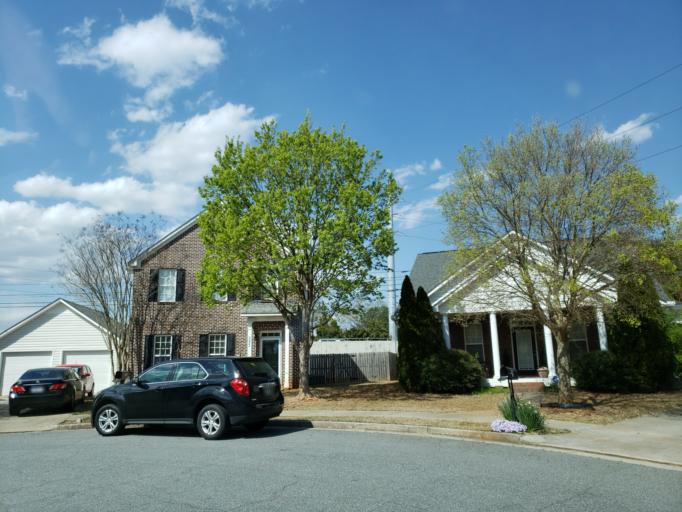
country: US
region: Georgia
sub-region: Cobb County
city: Kennesaw
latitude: 34.0334
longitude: -84.5508
